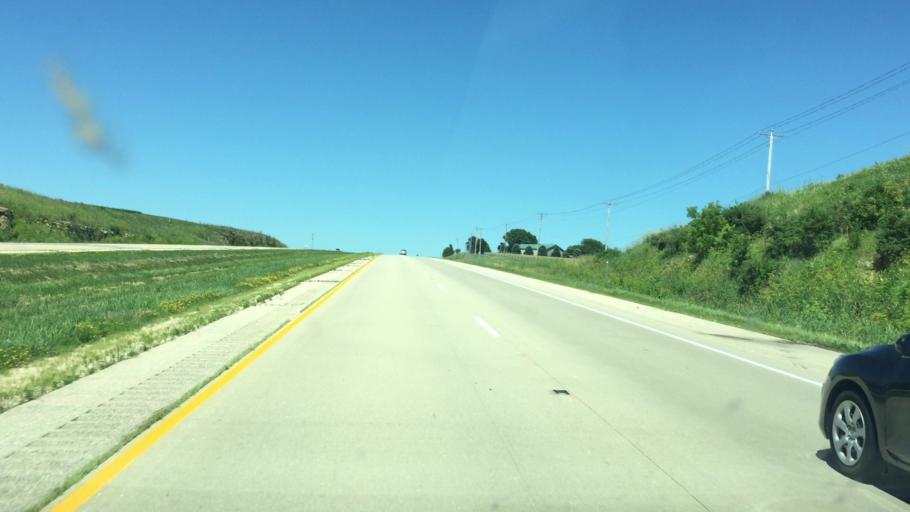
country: US
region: Wisconsin
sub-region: Iowa County
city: Mineral Point
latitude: 42.8296
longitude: -90.2335
